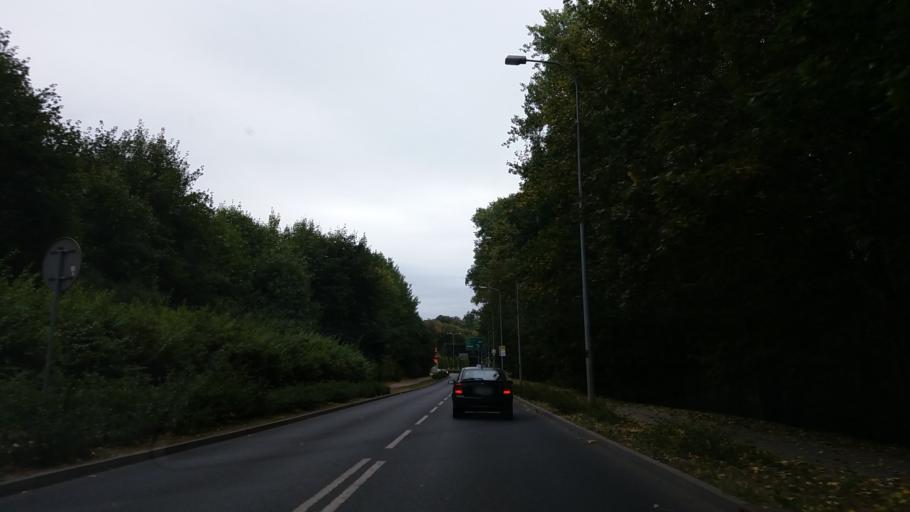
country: PL
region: Lubusz
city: Gorzow Wielkopolski
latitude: 52.7598
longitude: 15.2332
